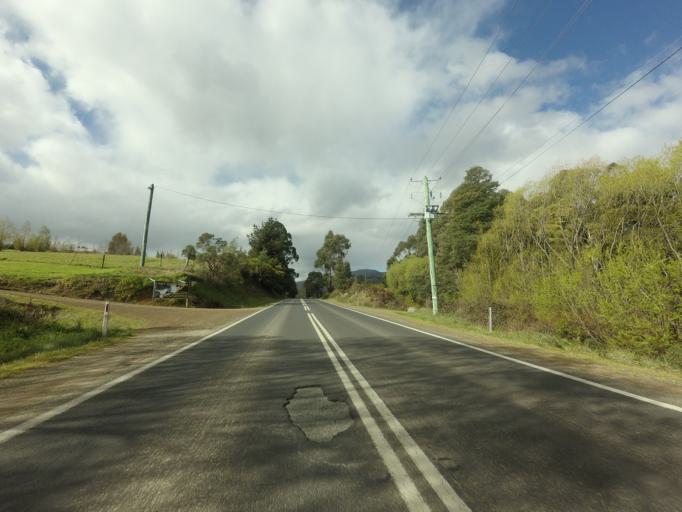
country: AU
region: Tasmania
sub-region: Huon Valley
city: Franklin
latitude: -43.0714
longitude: 147.0201
